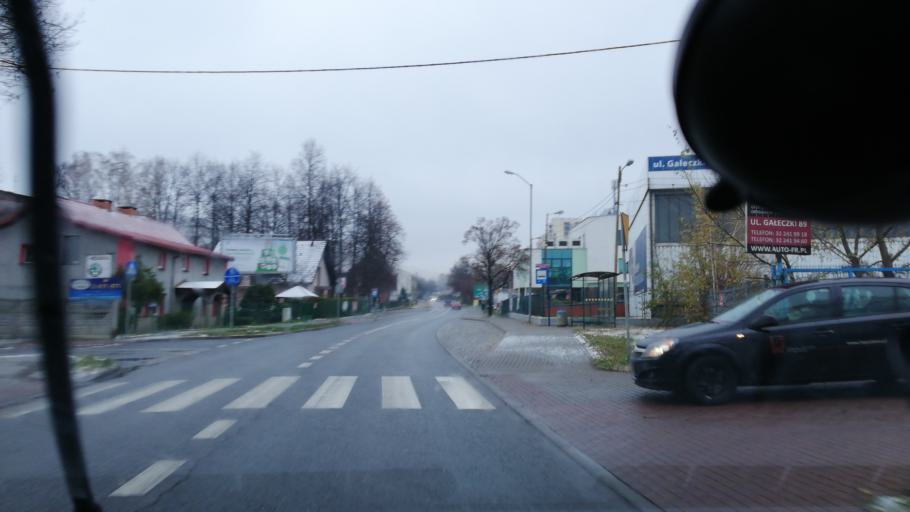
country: PL
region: Silesian Voivodeship
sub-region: Chorzow
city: Chorzow
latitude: 50.2800
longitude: 18.9605
